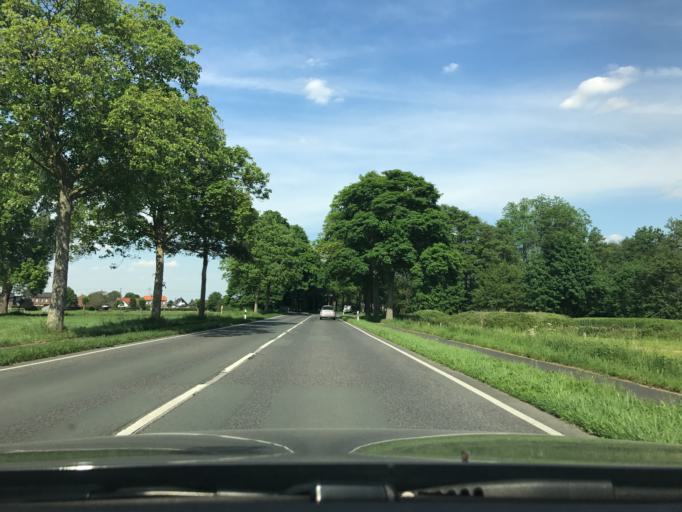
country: DE
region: North Rhine-Westphalia
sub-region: Regierungsbezirk Dusseldorf
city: Wachtendonk
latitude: 51.4357
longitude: 6.3914
